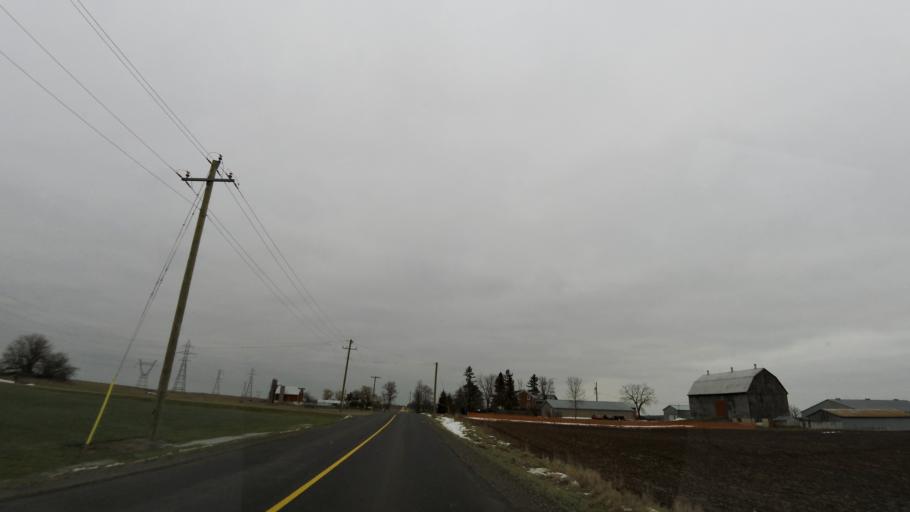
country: CA
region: Ontario
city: Brantford
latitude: 43.1083
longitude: -80.1798
